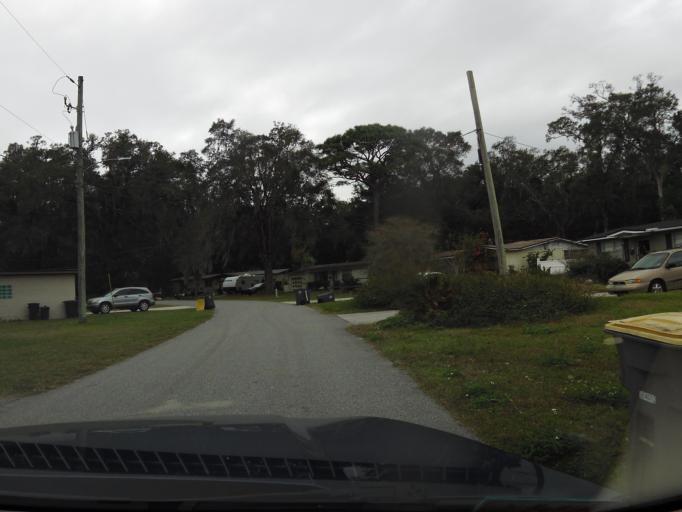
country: US
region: Florida
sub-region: Duval County
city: Jacksonville
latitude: 30.3091
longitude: -81.6043
